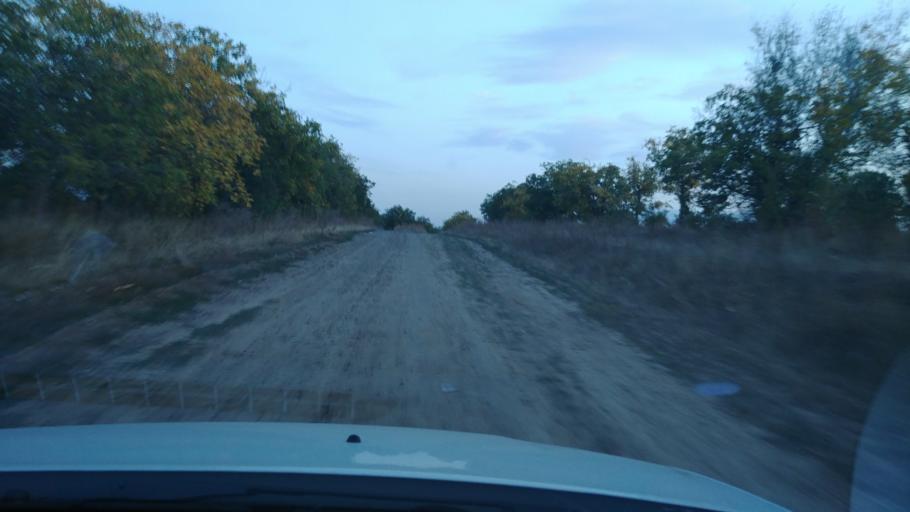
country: MD
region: Rezina
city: Saharna
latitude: 47.6827
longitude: 28.9079
